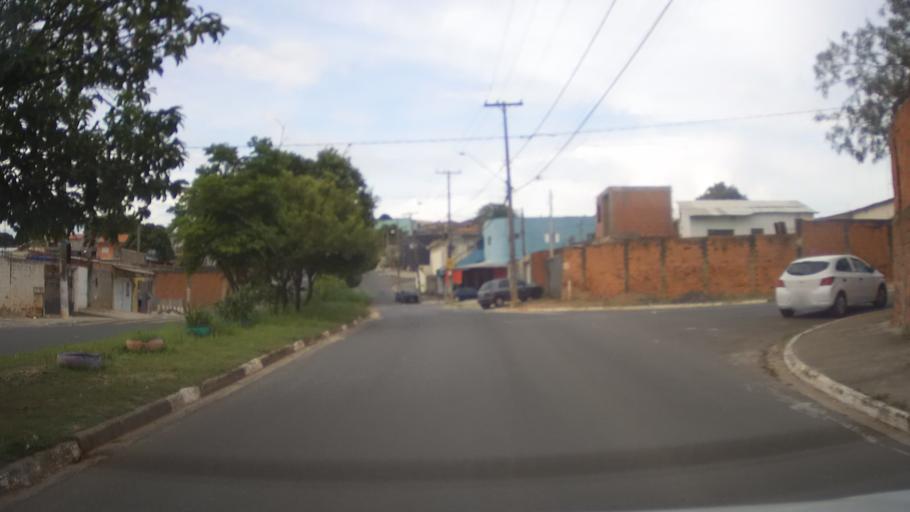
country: BR
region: Sao Paulo
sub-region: Hortolandia
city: Hortolandia
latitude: -22.9578
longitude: -47.1836
